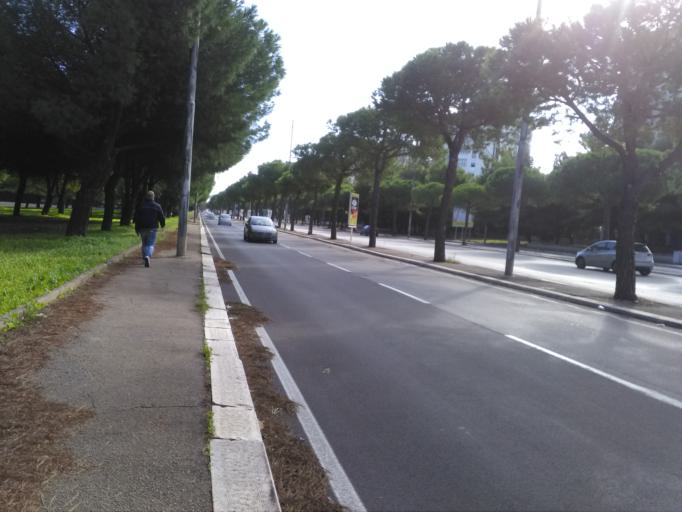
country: IT
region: Apulia
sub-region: Provincia di Bari
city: Bari
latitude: 41.1058
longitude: 16.9011
